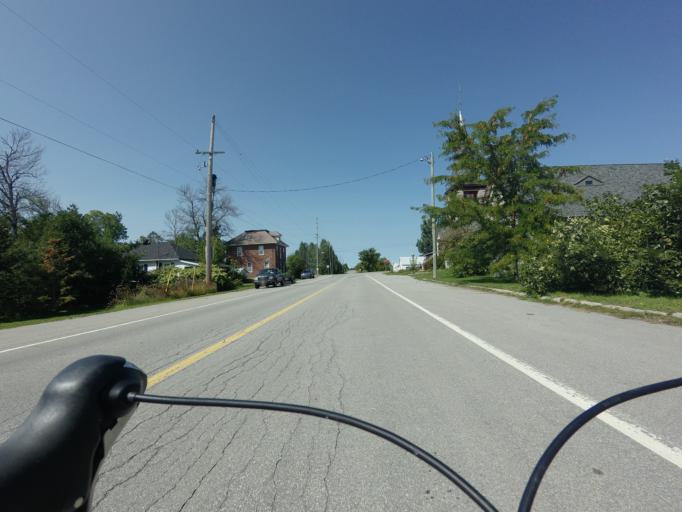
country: CA
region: Ontario
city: Arnprior
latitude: 45.4537
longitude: -76.0883
